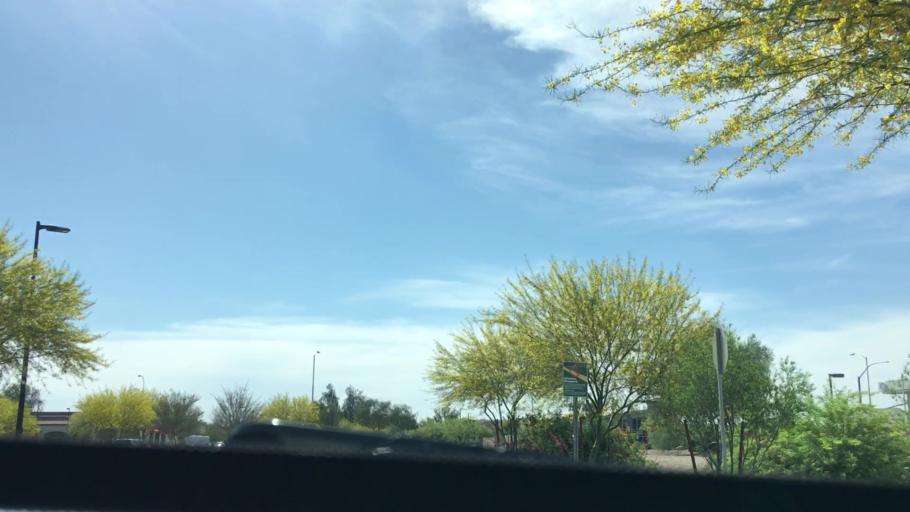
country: US
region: Arizona
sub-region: Maricopa County
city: Peoria
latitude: 33.6095
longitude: -112.2188
